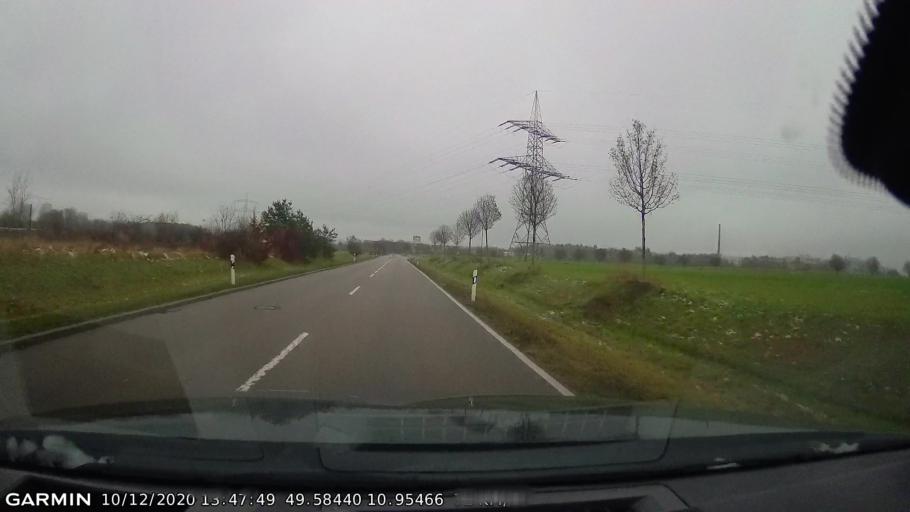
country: DE
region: Bavaria
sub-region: Regierungsbezirk Mittelfranken
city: Erlangen
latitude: 49.5844
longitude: 10.9548
